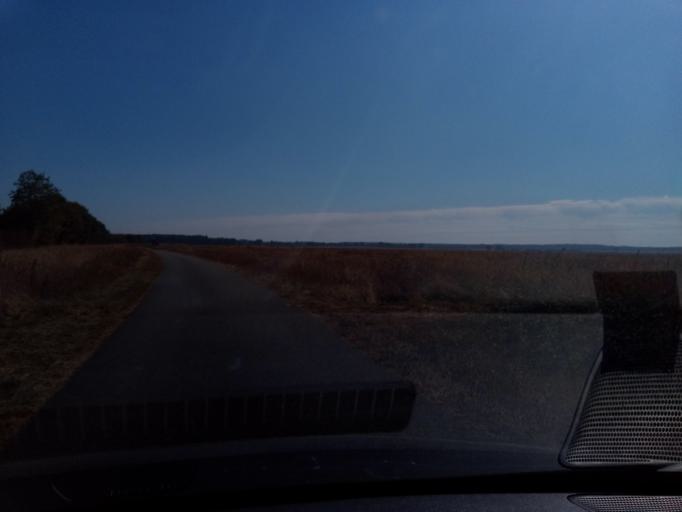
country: FR
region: Poitou-Charentes
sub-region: Departement de la Vienne
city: Lussac-les-Chateaux
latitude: 46.3826
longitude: 0.7762
